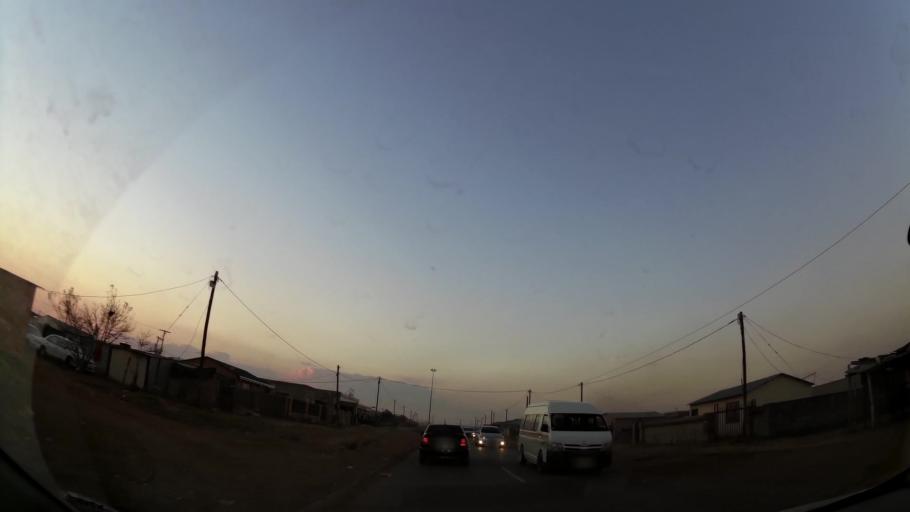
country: ZA
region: Gauteng
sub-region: Ekurhuleni Metropolitan Municipality
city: Nigel
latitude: -26.3624
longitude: 28.3929
